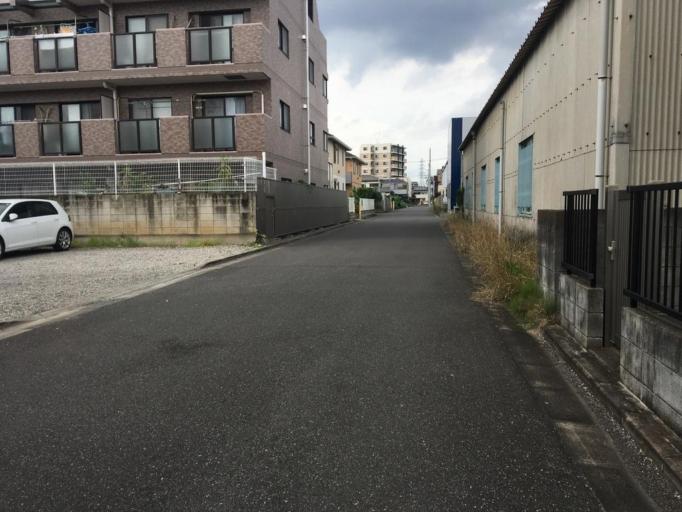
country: JP
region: Saitama
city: Shimotoda
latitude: 35.8191
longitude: 139.6610
